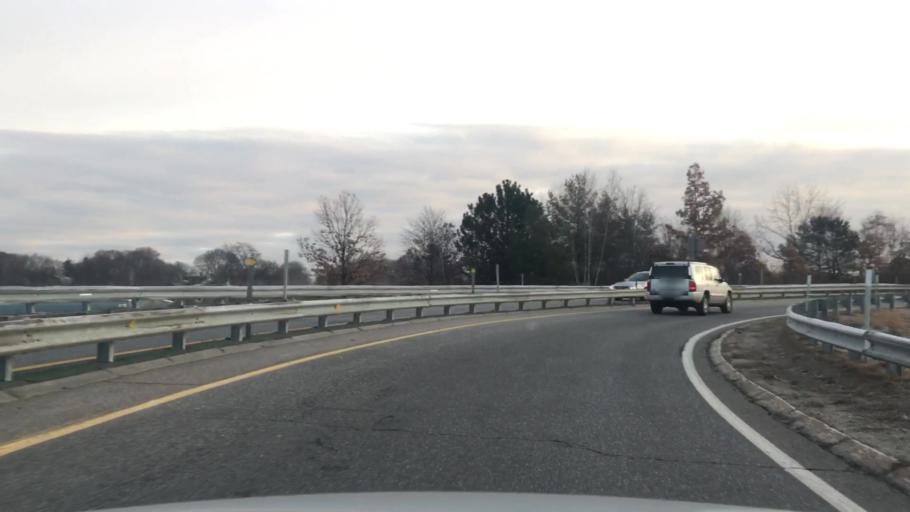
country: US
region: Maine
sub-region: Cumberland County
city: Portland
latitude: 43.6572
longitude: -70.2857
